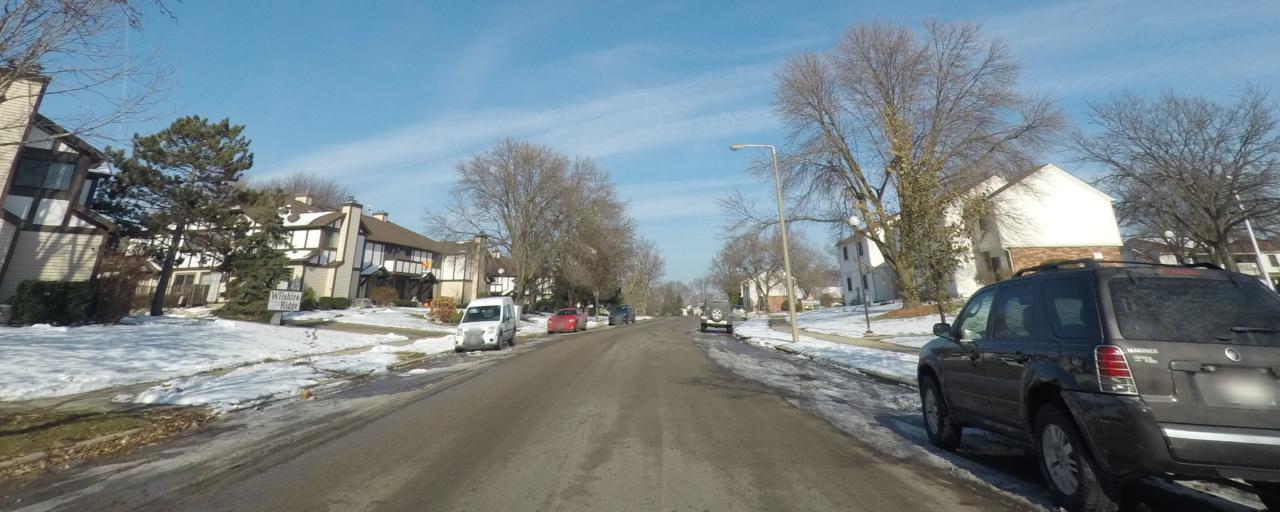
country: US
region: Wisconsin
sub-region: Dane County
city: Madison
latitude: 43.0274
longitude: -89.4149
